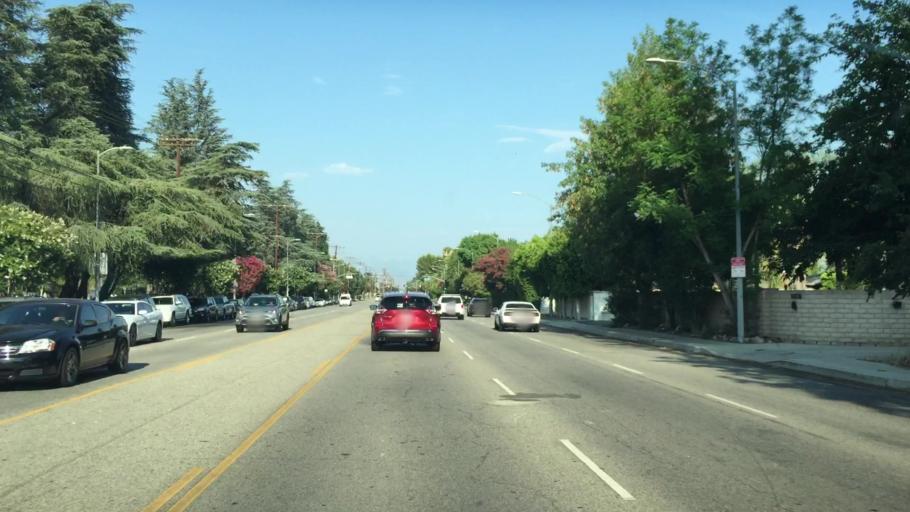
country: US
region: California
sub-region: Los Angeles County
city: Northridge
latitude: 34.2358
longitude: -118.5092
